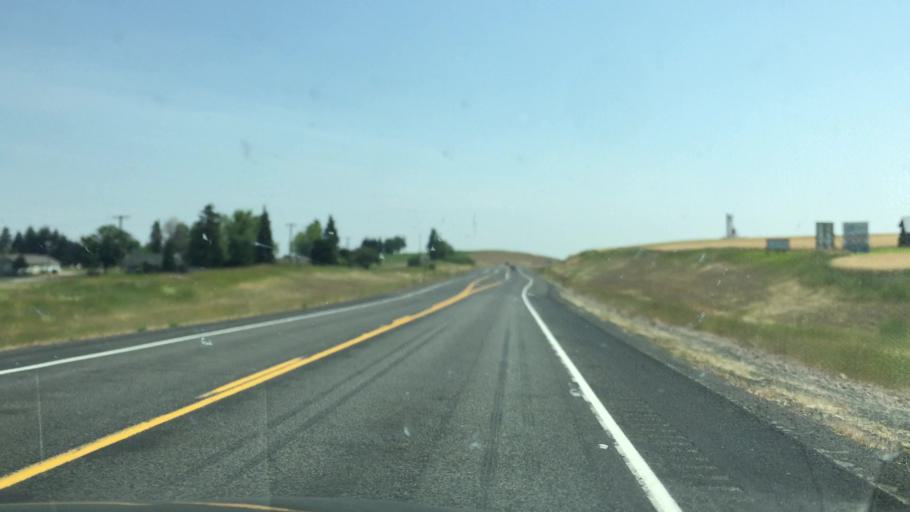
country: US
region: Idaho
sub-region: Lewis County
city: Nezperce
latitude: 46.2377
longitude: -116.4763
